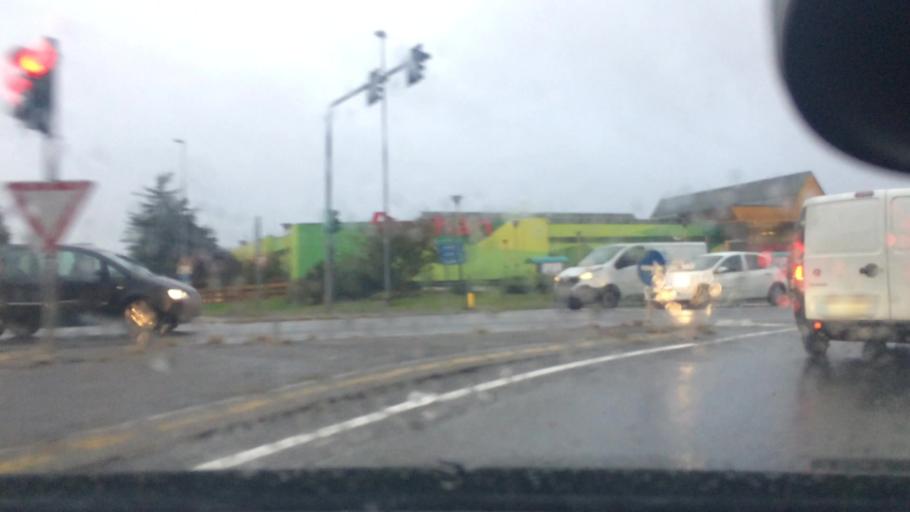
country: IT
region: Lombardy
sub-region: Citta metropolitana di Milano
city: Nerviano
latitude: 45.5526
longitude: 8.9849
